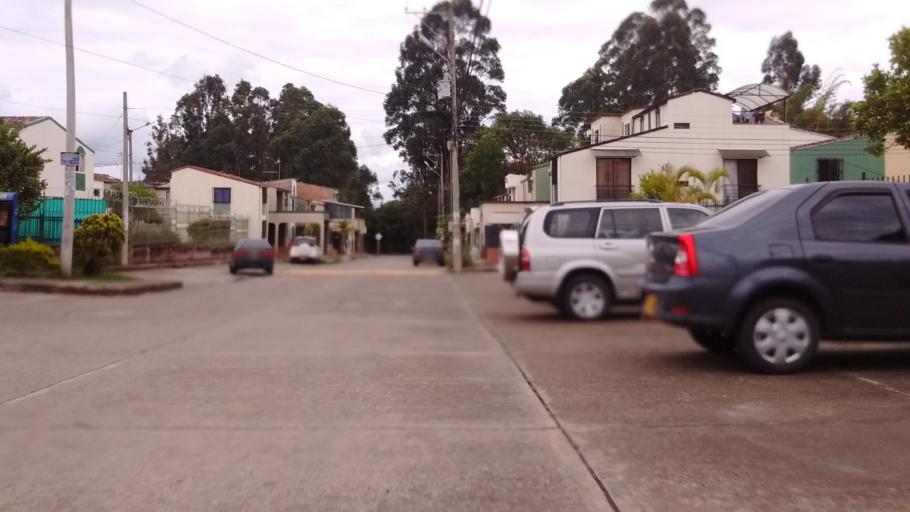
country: CO
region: Cauca
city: Popayan
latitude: 2.4807
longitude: -76.5766
